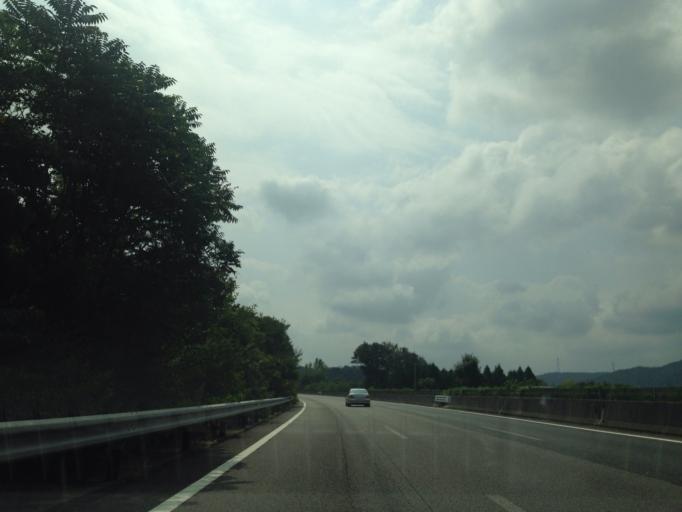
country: JP
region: Aichi
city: Gamagori
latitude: 34.9057
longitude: 137.2500
